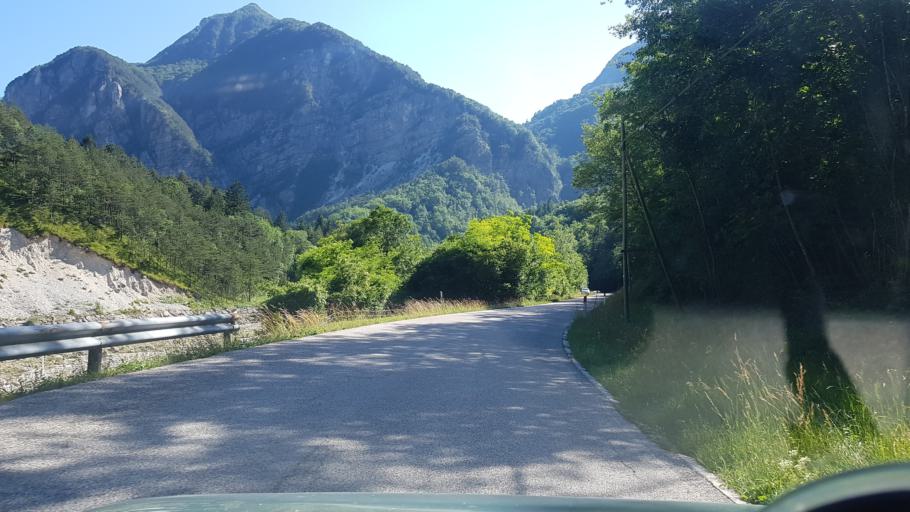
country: IT
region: Friuli Venezia Giulia
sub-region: Provincia di Udine
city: Moggio Udinese
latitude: 46.4557
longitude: 13.1905
